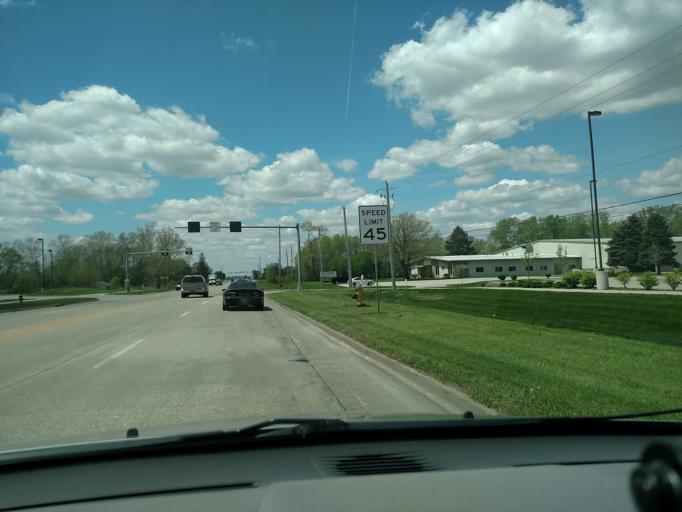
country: US
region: Iowa
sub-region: Polk County
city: Ankeny
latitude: 41.7029
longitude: -93.5880
